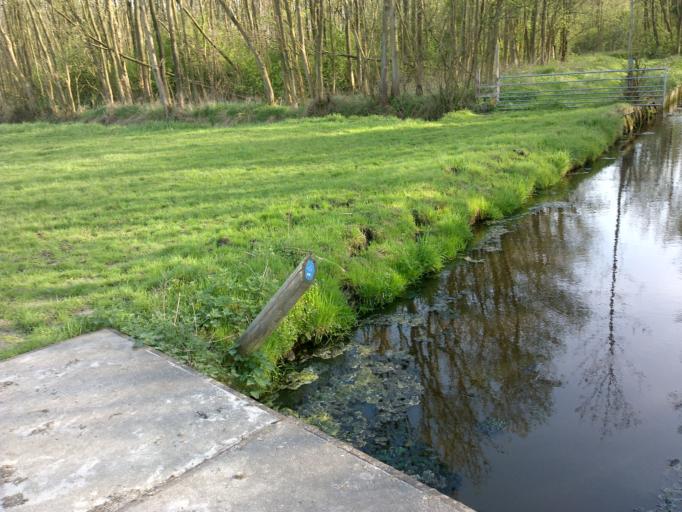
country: NL
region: South Holland
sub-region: Gemeente Noordwijkerhout
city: Noordwijkerhout
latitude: 52.2560
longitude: 4.5225
